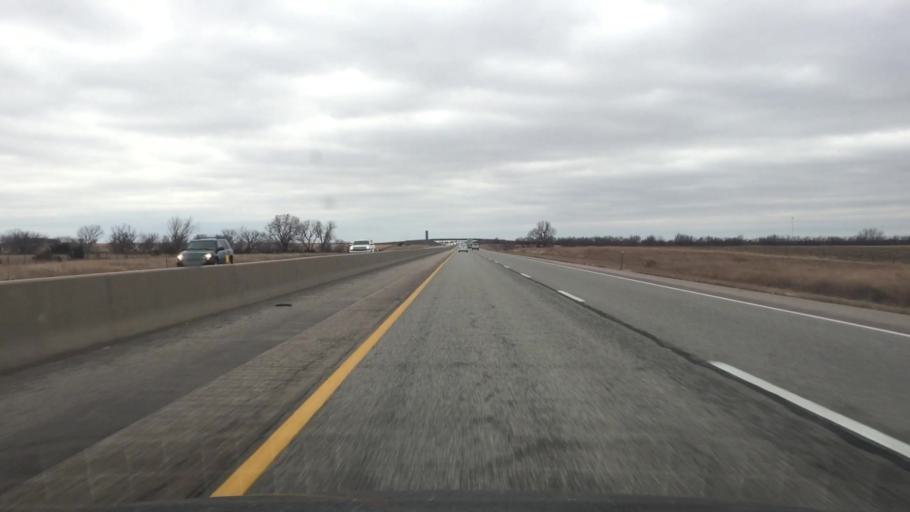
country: US
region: Kansas
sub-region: Butler County
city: El Dorado
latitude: 38.0203
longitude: -96.6689
